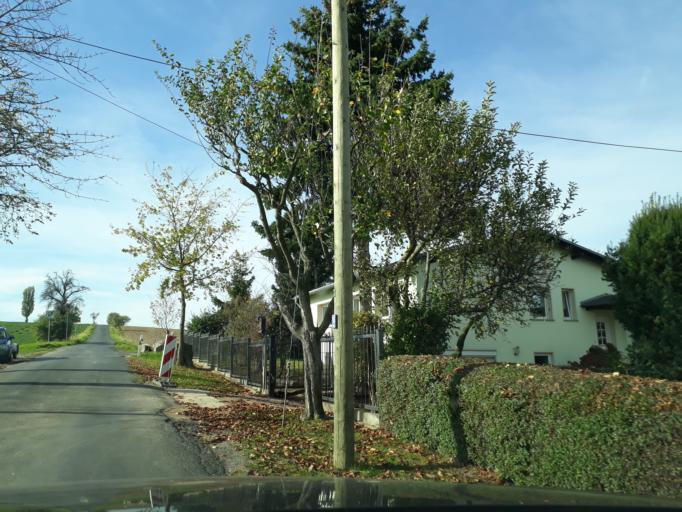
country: DE
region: Saxony
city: Niederstriegis
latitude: 51.1080
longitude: 13.1580
